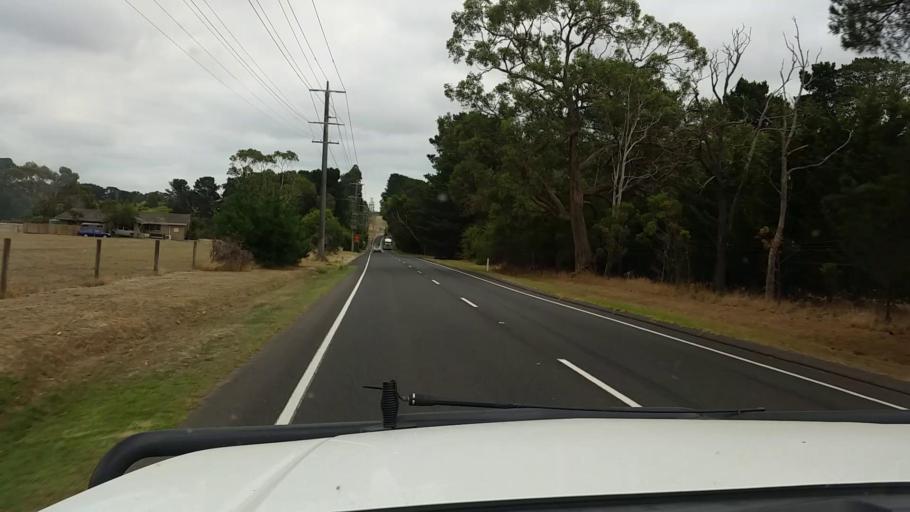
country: AU
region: Victoria
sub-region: Mornington Peninsula
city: Moorooduc
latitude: -38.2816
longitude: 145.1170
